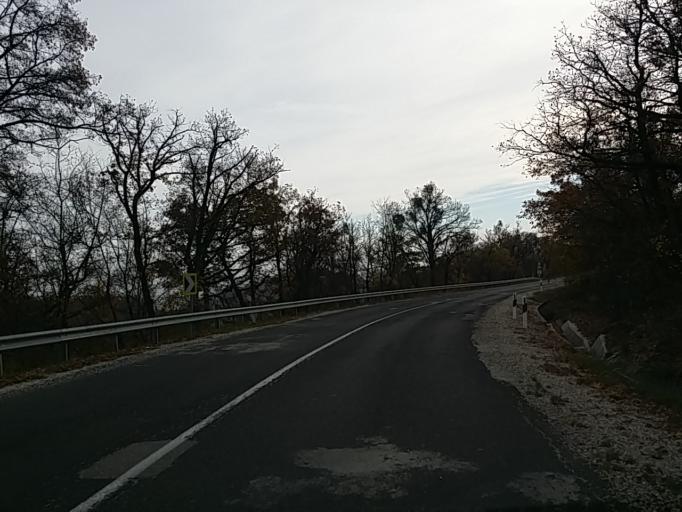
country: HU
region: Heves
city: Gyongyossolymos
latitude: 47.8438
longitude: 19.9603
